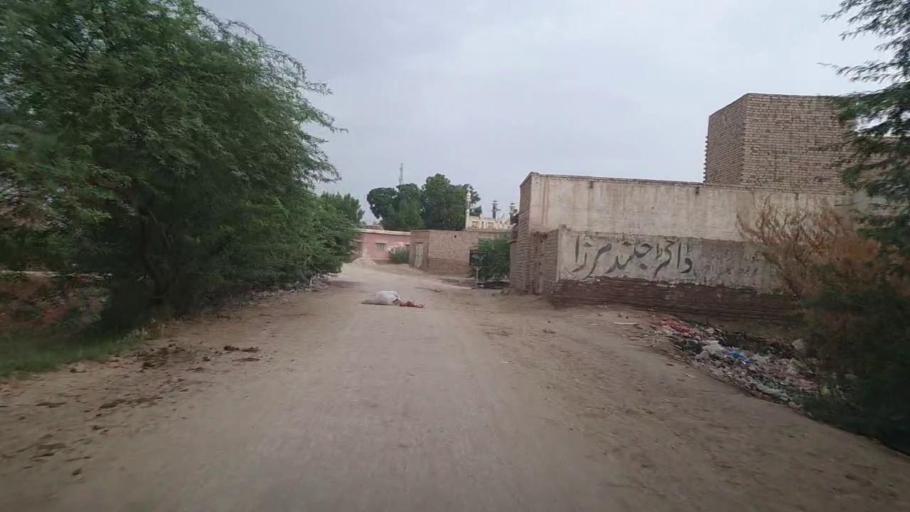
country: PK
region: Sindh
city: Karaundi
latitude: 26.9921
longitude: 68.3437
